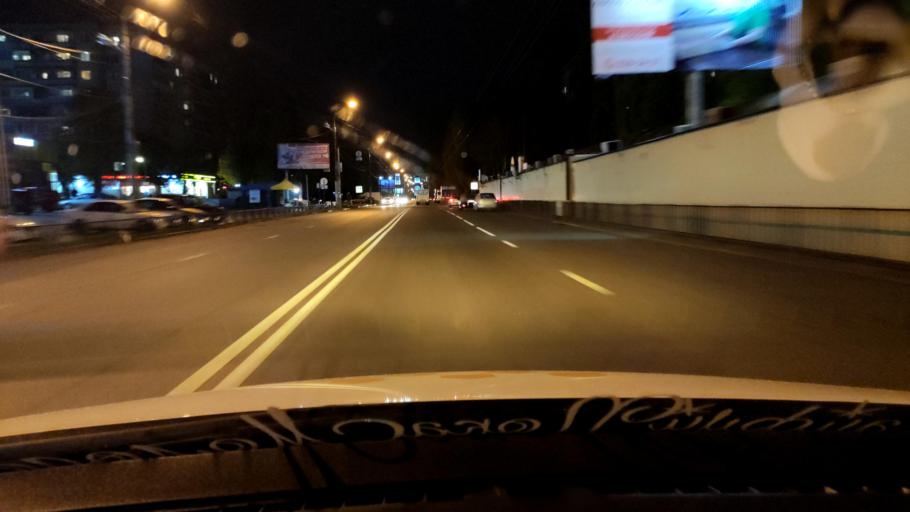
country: RU
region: Voronezj
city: Podgornoye
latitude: 51.7075
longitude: 39.1741
